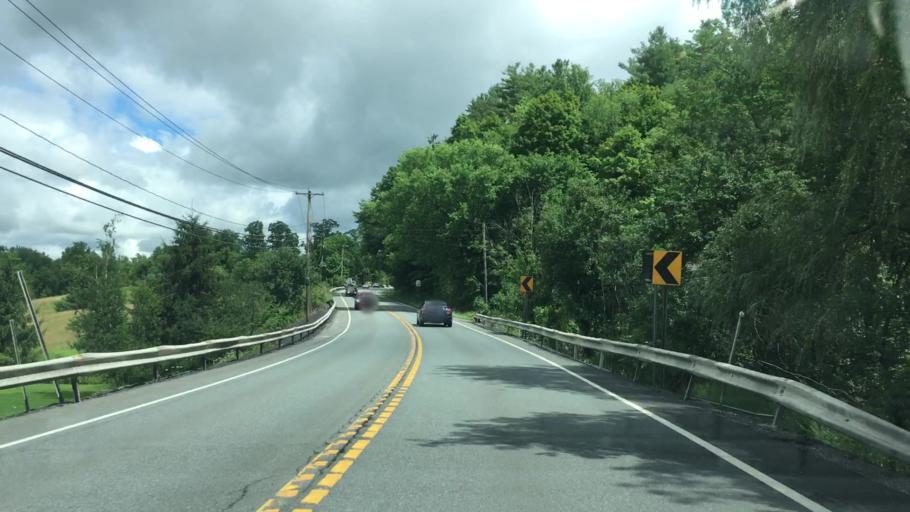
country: US
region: New York
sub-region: Rensselaer County
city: Hoosick Falls
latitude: 42.8453
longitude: -73.4497
